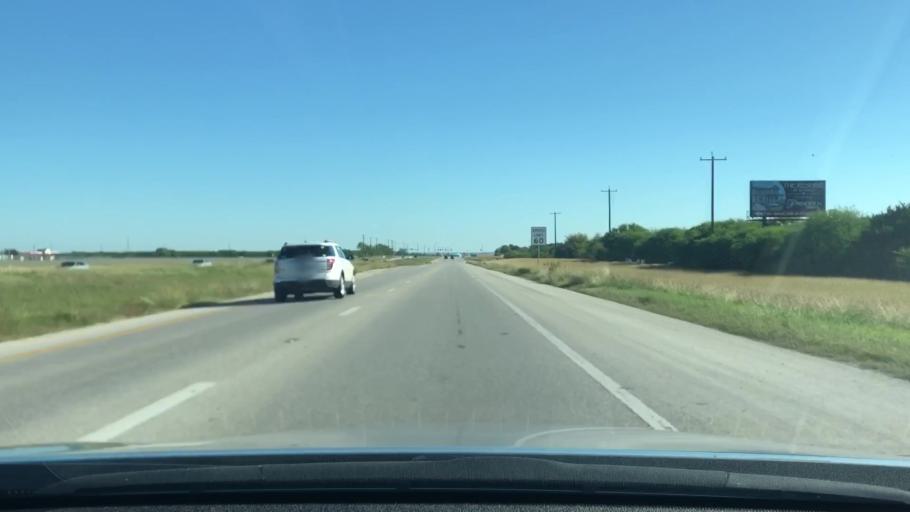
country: US
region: Texas
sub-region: Bexar County
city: Converse
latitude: 29.5190
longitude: -98.2919
